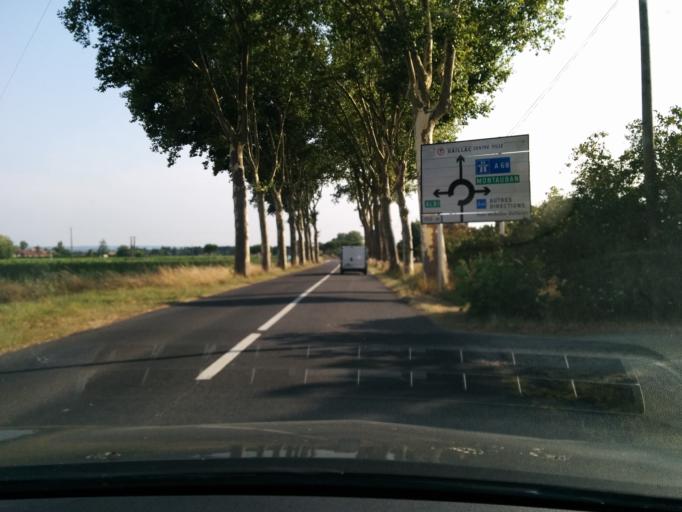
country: FR
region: Midi-Pyrenees
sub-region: Departement du Tarn
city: Gaillac
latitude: 43.9293
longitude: 1.9140
